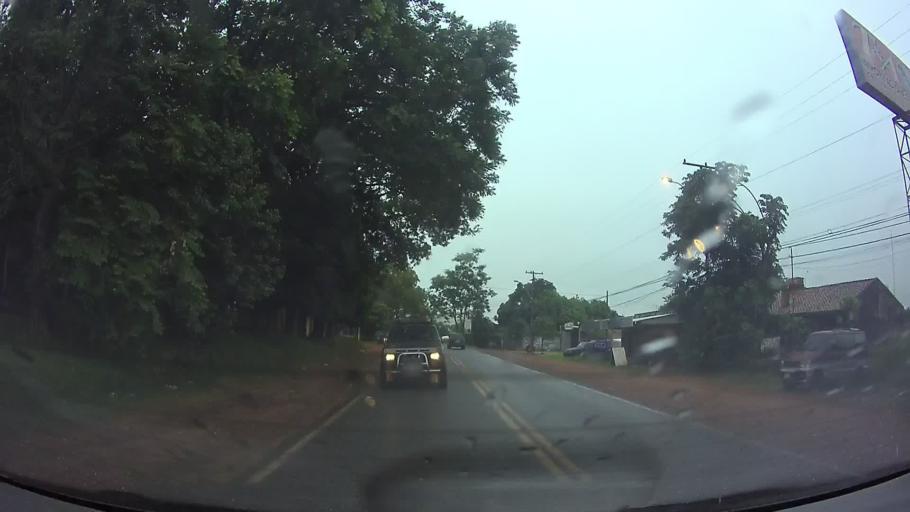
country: PY
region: Central
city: Ita
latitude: -25.5028
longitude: -57.3571
